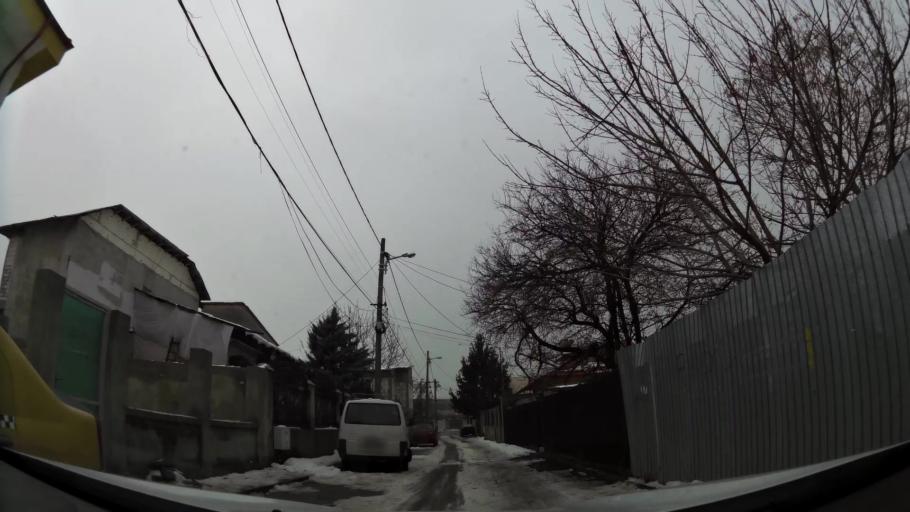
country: RO
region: Ilfov
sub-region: Comuna Popesti-Leordeni
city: Popesti-Leordeni
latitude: 44.4049
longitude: 26.1461
